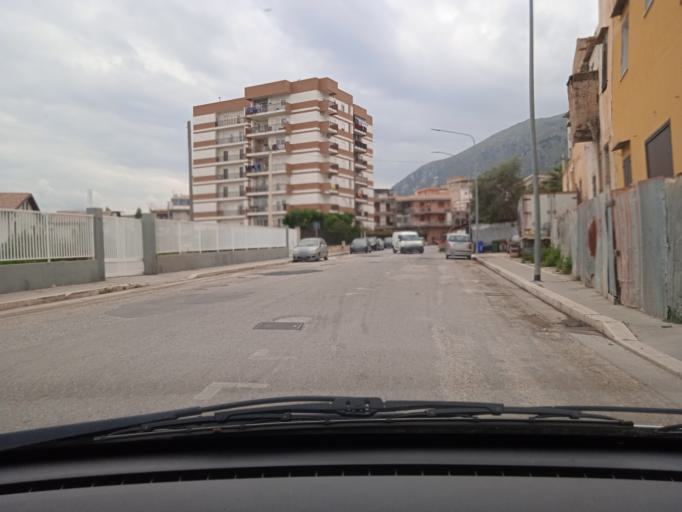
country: IT
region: Sicily
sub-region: Palermo
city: Portella di Mare
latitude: 38.0760
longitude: 13.4535
